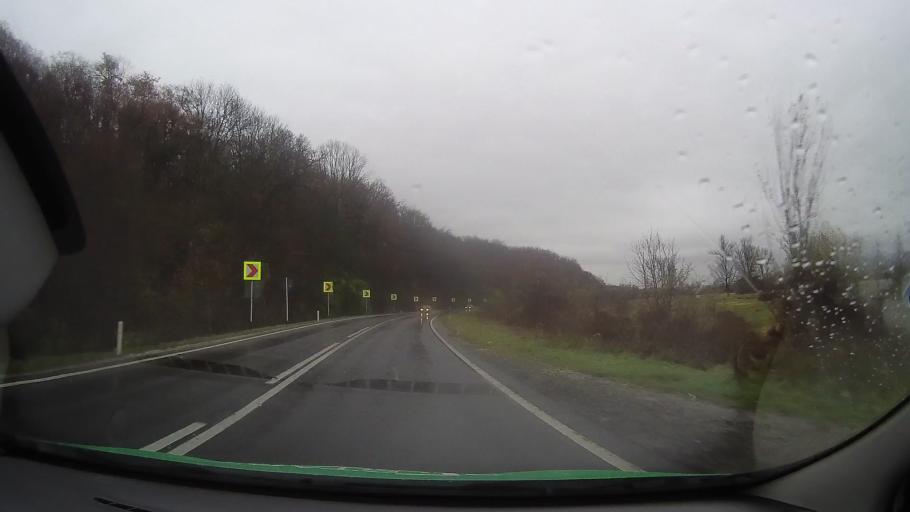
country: RO
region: Mures
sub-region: Comuna Brancovenesti
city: Brancovenesti
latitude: 46.8660
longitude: 24.7684
